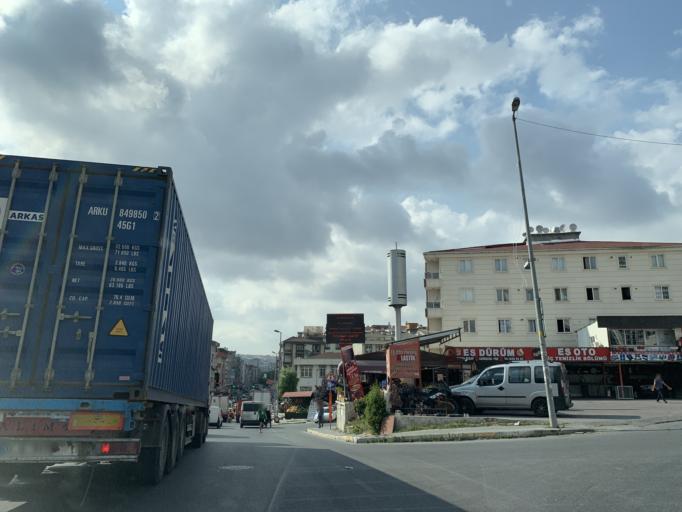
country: TR
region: Istanbul
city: Esenyurt
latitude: 41.0203
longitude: 28.6755
